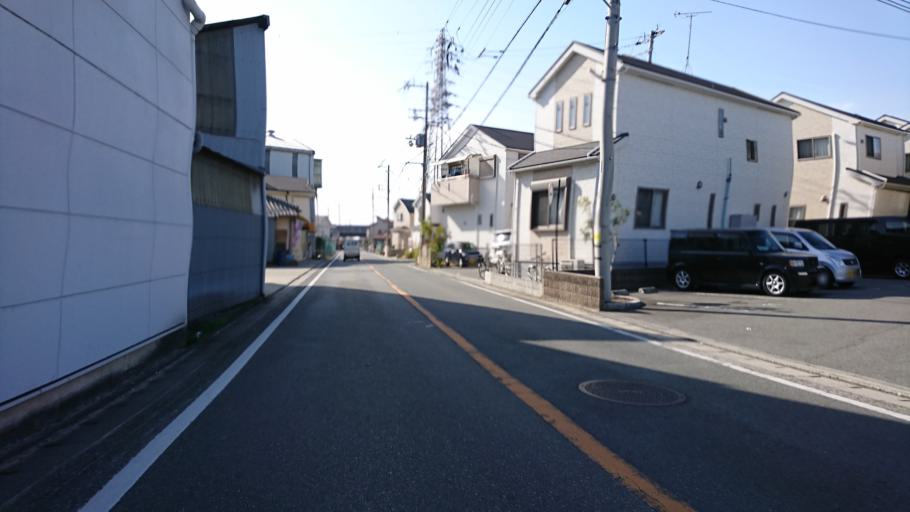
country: JP
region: Hyogo
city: Kakogawacho-honmachi
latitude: 34.7240
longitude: 134.8648
